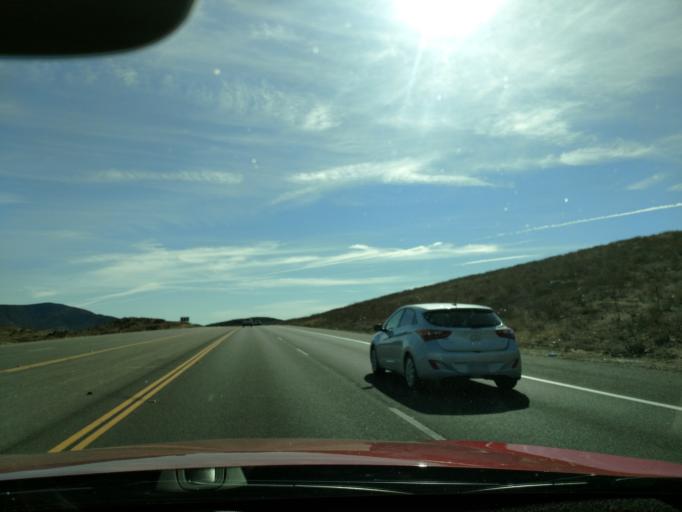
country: US
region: California
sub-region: Riverside County
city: Winchester
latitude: 33.6494
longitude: -117.0843
